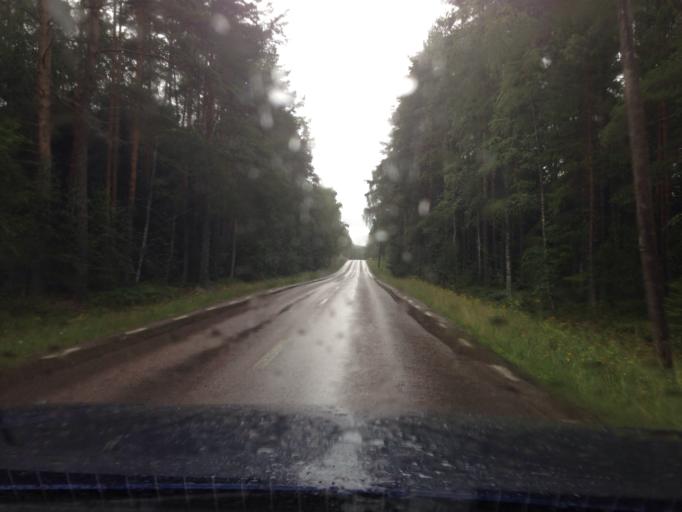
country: SE
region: Dalarna
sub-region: Ludvika Kommun
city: Grangesberg
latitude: 60.1574
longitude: 14.9734
